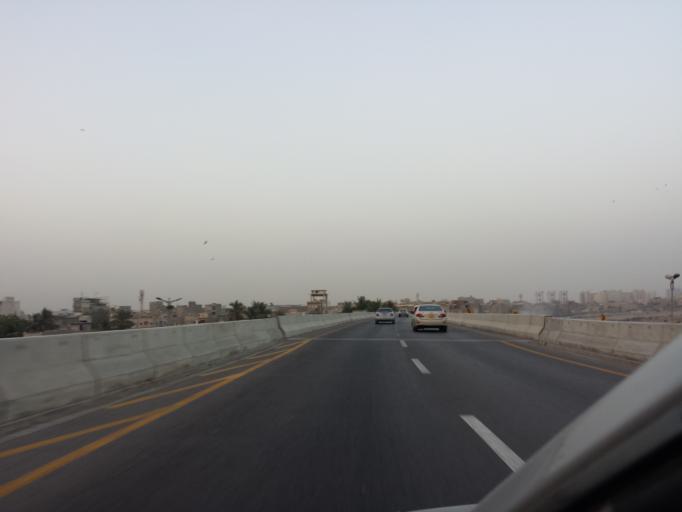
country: PK
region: Sindh
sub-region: Karachi District
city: Karachi
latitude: 24.9068
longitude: 67.0635
